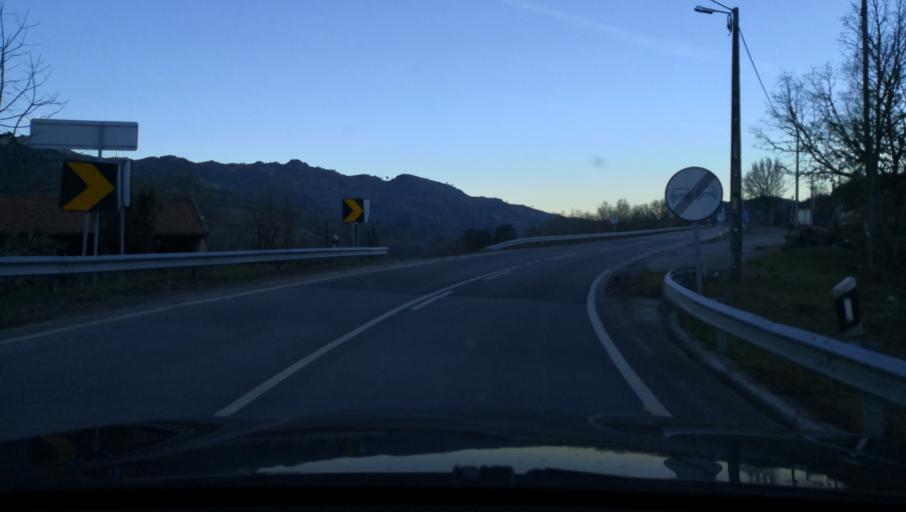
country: PT
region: Vila Real
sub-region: Vila Pouca de Aguiar
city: Vila Pouca de Aguiar
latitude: 41.4207
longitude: -7.6852
